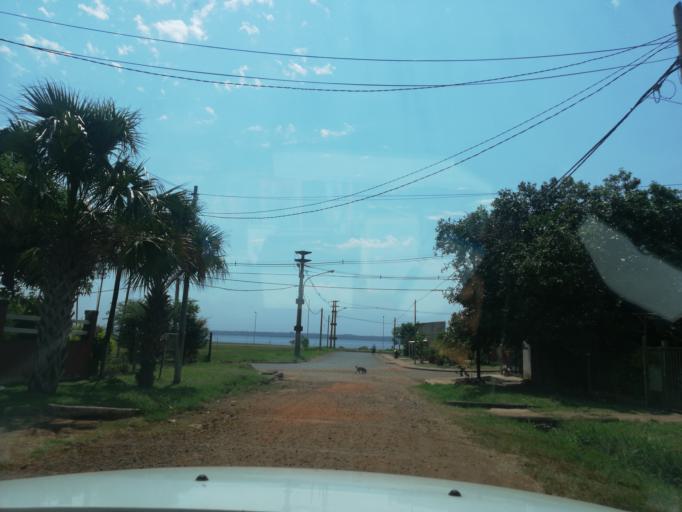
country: AR
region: Misiones
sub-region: Departamento de Capital
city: Posadas
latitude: -27.4262
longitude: -55.8750
